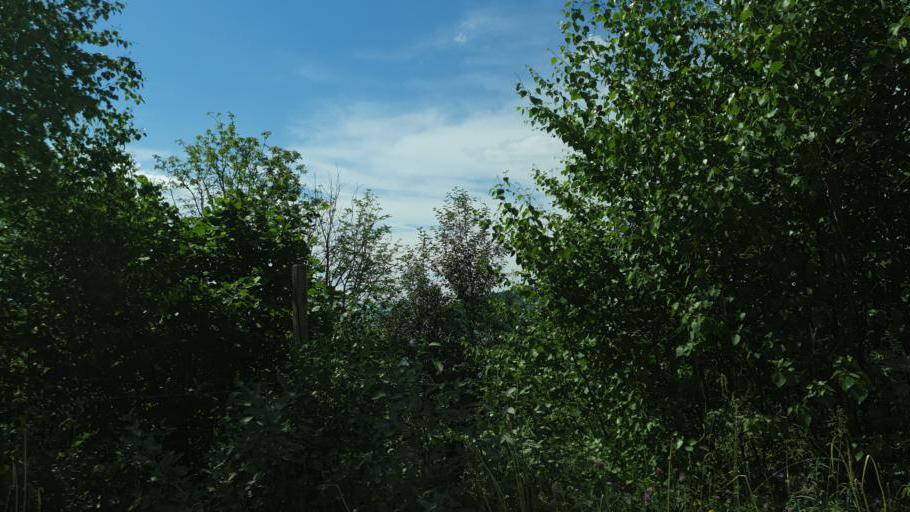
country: NO
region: Nord-Trondelag
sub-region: Leksvik
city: Leksvik
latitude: 63.6781
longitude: 10.6566
